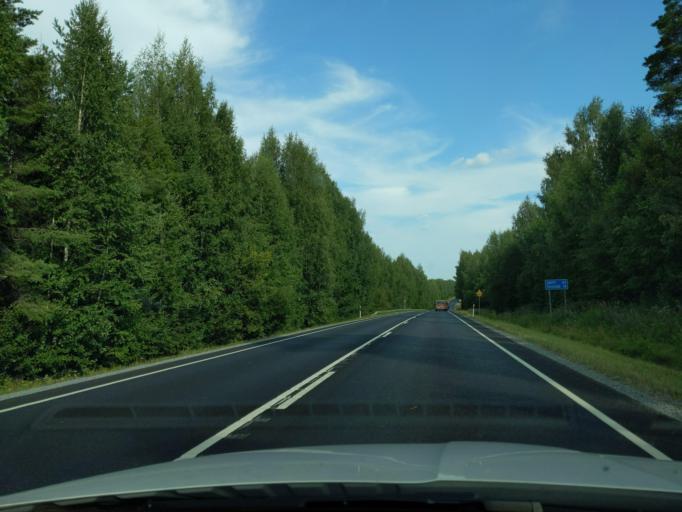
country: FI
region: Haeme
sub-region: Haemeenlinna
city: Hauho
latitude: 61.1718
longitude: 24.6161
